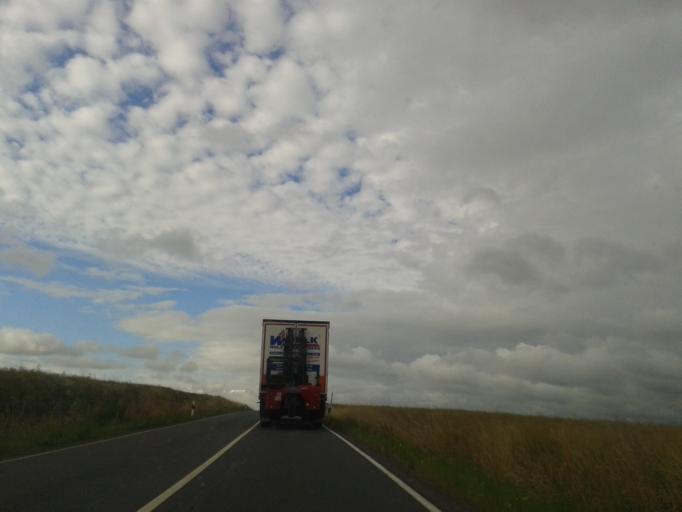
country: DE
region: Saxony
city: Reinsberg
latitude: 51.0341
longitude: 13.3466
